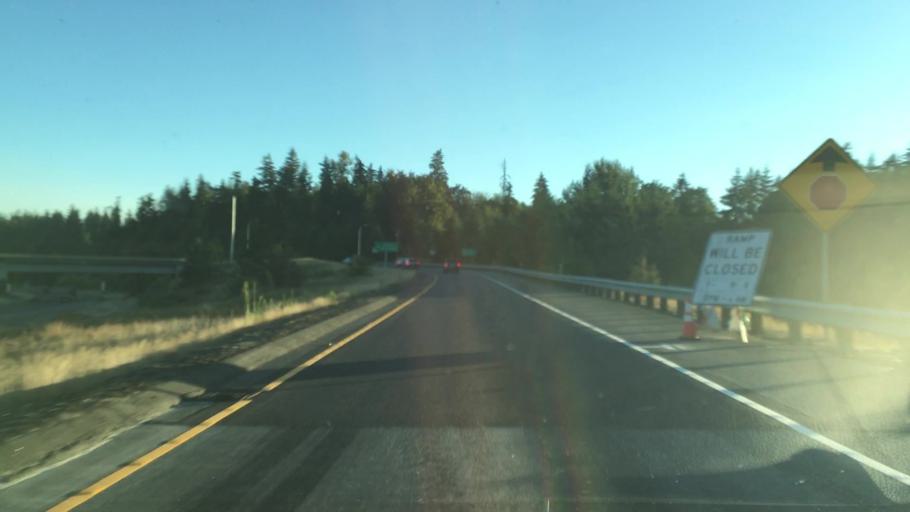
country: US
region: Washington
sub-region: King County
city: Lea Hill
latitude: 47.3321
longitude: -122.1569
